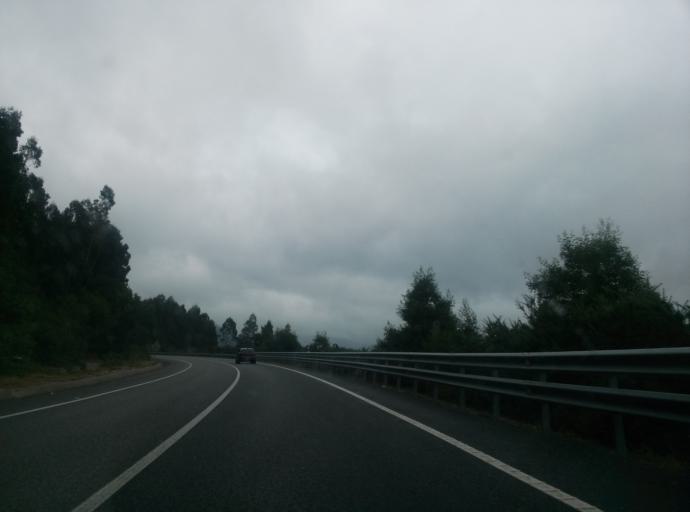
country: ES
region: Galicia
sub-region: Provincia de Lugo
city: Viveiro
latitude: 43.5601
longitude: -7.6439
